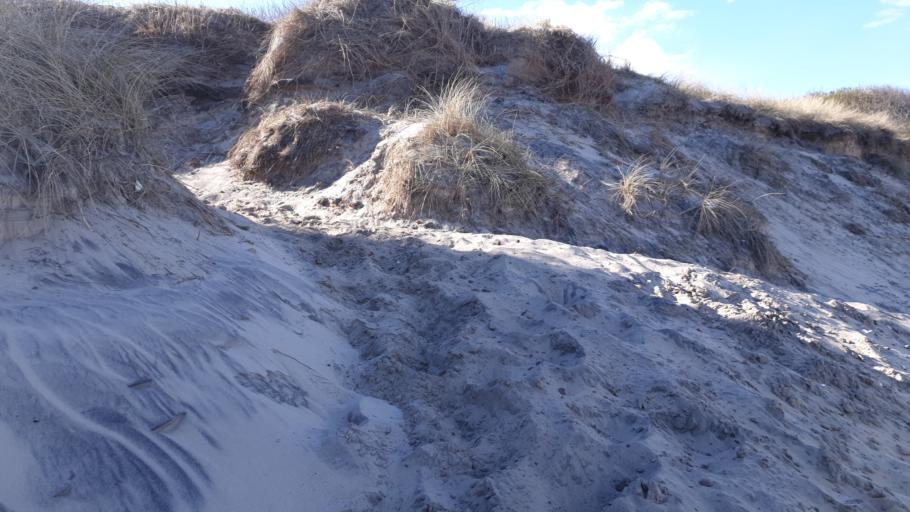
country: DK
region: North Denmark
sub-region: Hjorring Kommune
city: Hjorring
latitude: 57.4955
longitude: 9.8327
